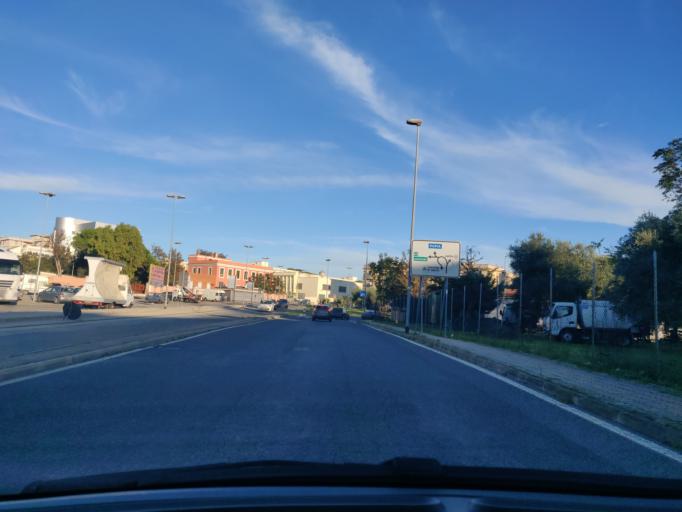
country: IT
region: Latium
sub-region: Citta metropolitana di Roma Capitale
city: Civitavecchia
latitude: 42.0995
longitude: 11.7978
